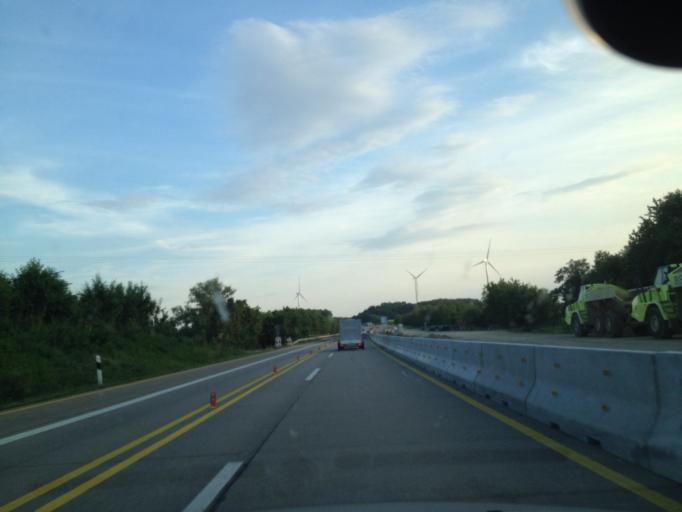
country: DE
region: Bavaria
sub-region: Regierungsbezirk Mittelfranken
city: Gollhofen
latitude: 49.5650
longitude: 10.1701
